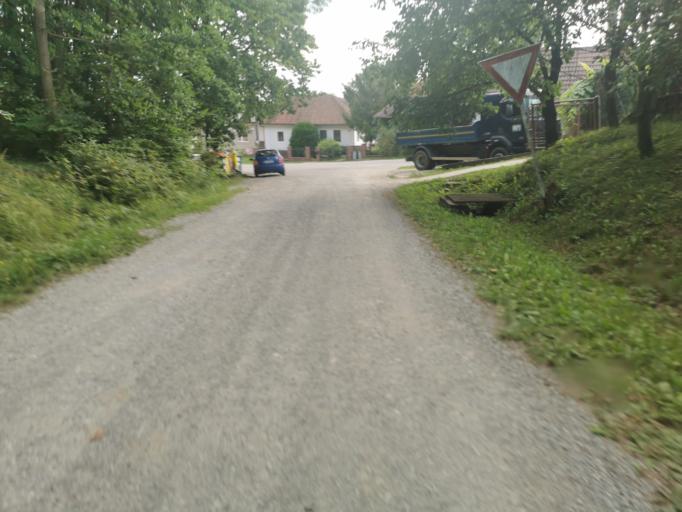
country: SK
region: Trenciansky
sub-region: Okres Myjava
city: Myjava
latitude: 48.7836
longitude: 17.6071
